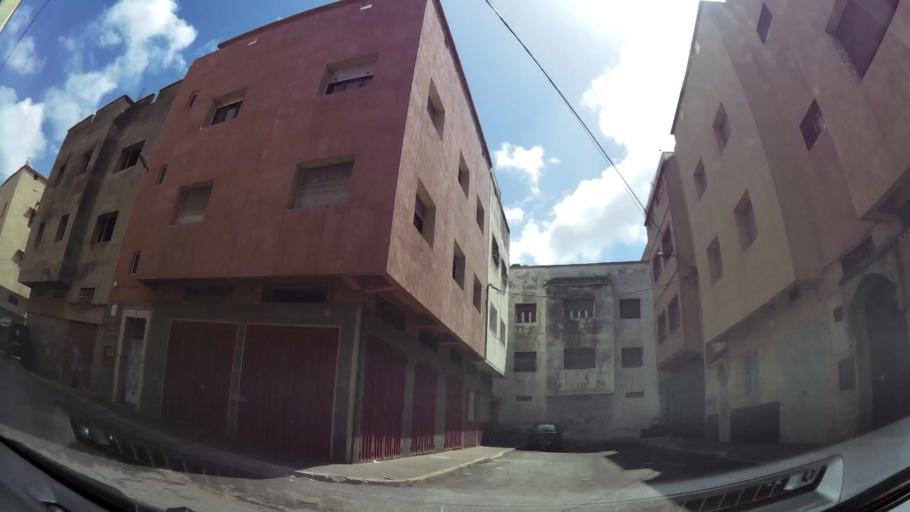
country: MA
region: Grand Casablanca
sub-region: Casablanca
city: Casablanca
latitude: 33.5398
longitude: -7.5913
